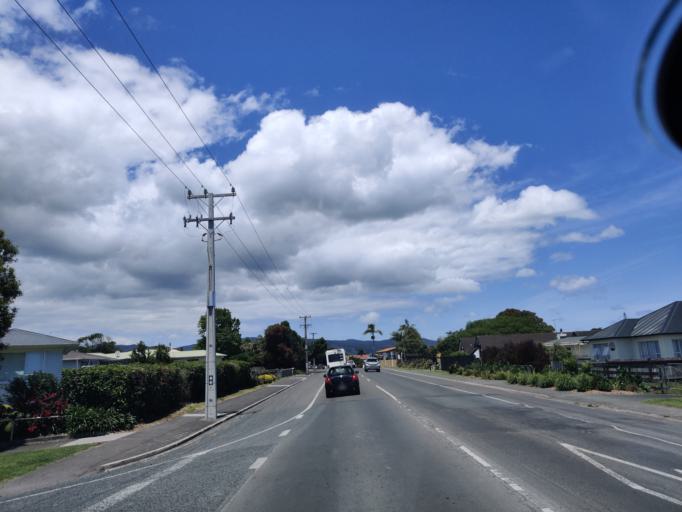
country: NZ
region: Northland
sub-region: Far North District
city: Kaitaia
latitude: -35.1045
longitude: 173.2589
